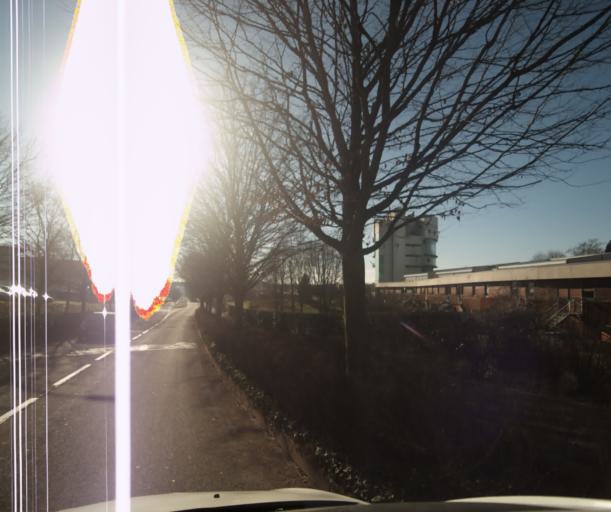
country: FR
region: Franche-Comte
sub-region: Departement du Doubs
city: Besancon
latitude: 47.2541
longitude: 6.0022
